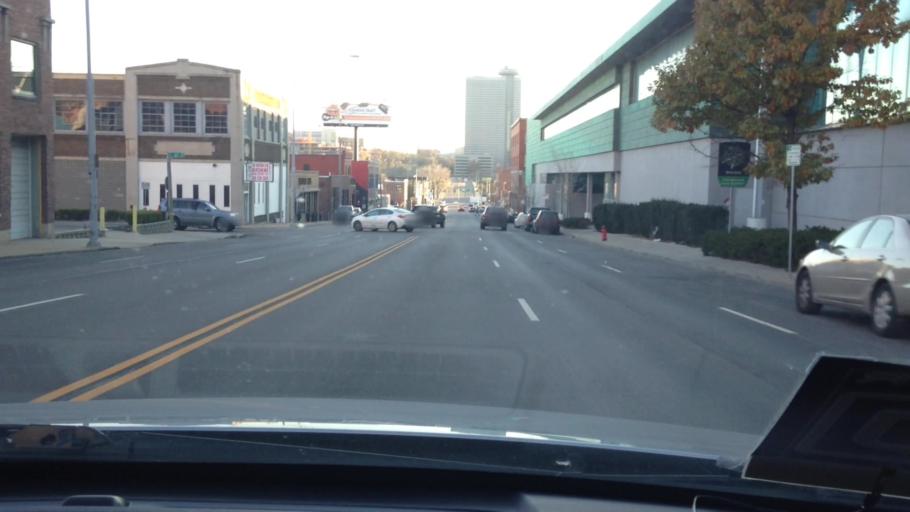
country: US
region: Missouri
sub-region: Jackson County
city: Kansas City
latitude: 39.0949
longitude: -94.5788
